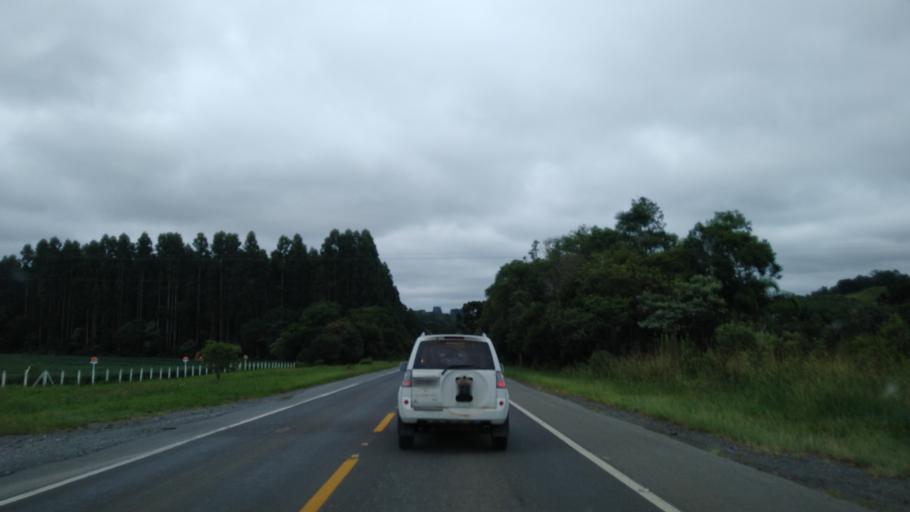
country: BR
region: Santa Catarina
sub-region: Tres Barras
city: Tres Barras
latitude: -26.1818
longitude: -50.2011
